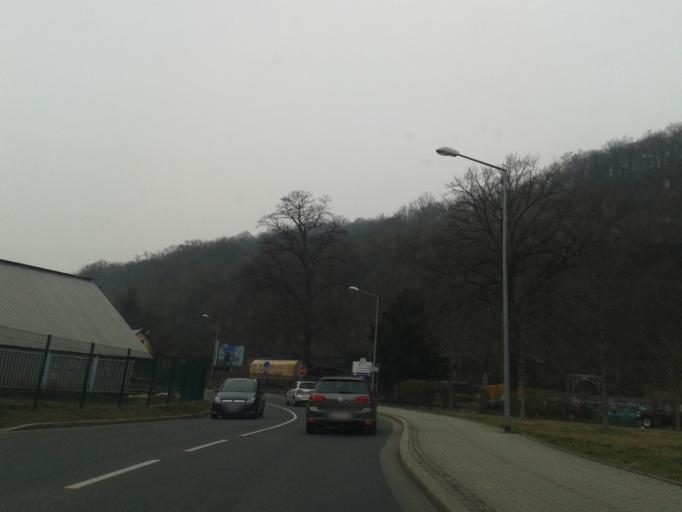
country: DE
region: Saxony
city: Freital
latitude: 51.0159
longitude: 13.6678
